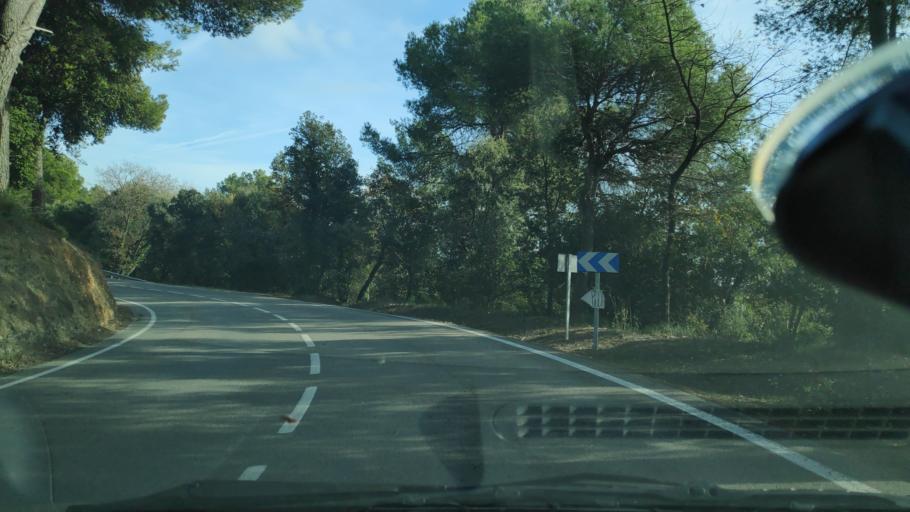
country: ES
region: Catalonia
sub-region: Provincia de Barcelona
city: Matadepera
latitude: 41.5967
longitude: 2.0433
